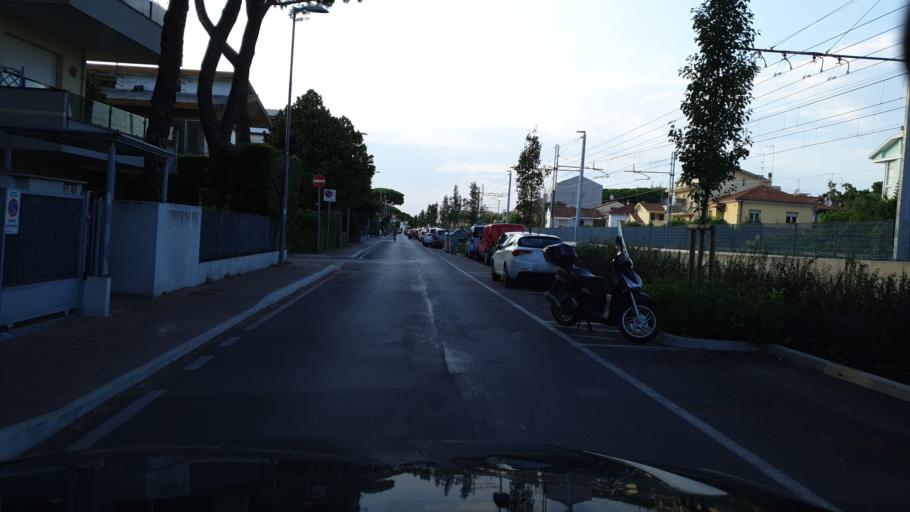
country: IT
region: Emilia-Romagna
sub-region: Provincia di Rimini
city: Riccione
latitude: 44.0076
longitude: 12.6474
